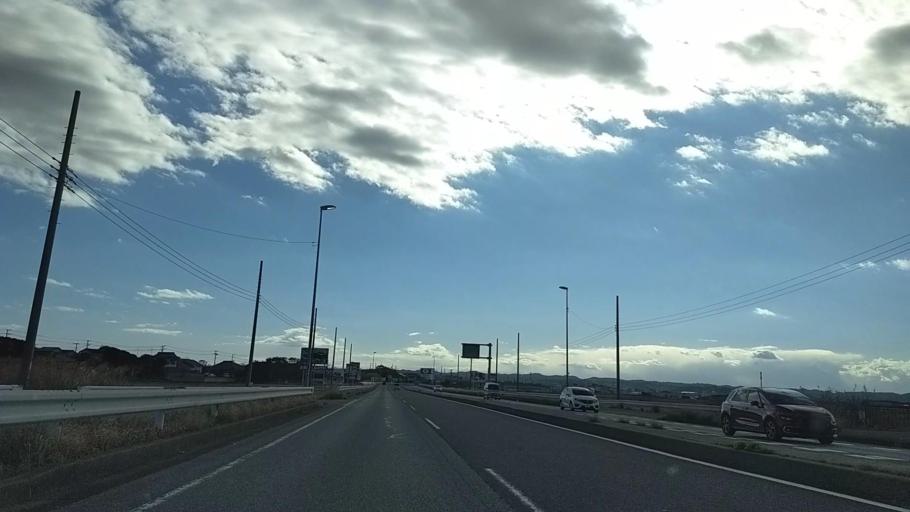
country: JP
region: Chiba
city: Tateyama
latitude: 35.0225
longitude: 139.8679
